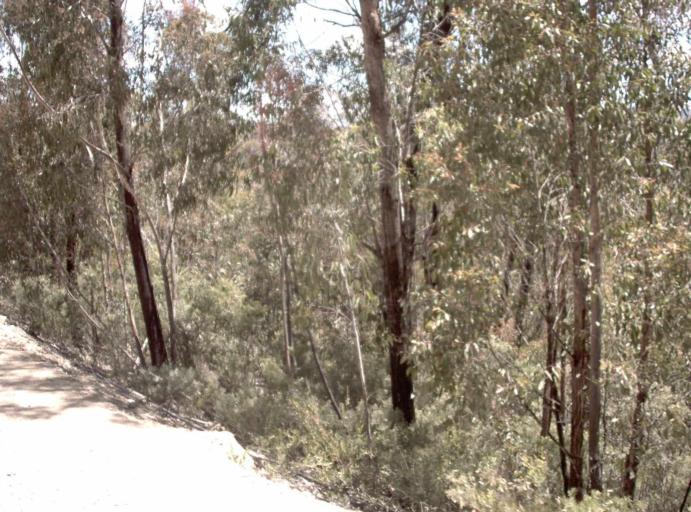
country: AU
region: New South Wales
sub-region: Snowy River
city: Jindabyne
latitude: -37.0756
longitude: 148.3280
